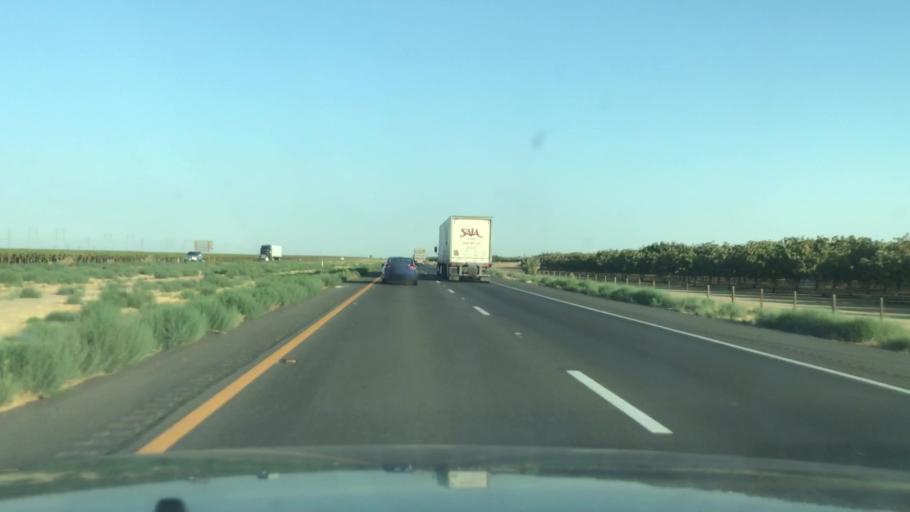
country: US
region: California
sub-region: Kings County
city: Kettleman City
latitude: 35.9216
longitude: -119.8991
